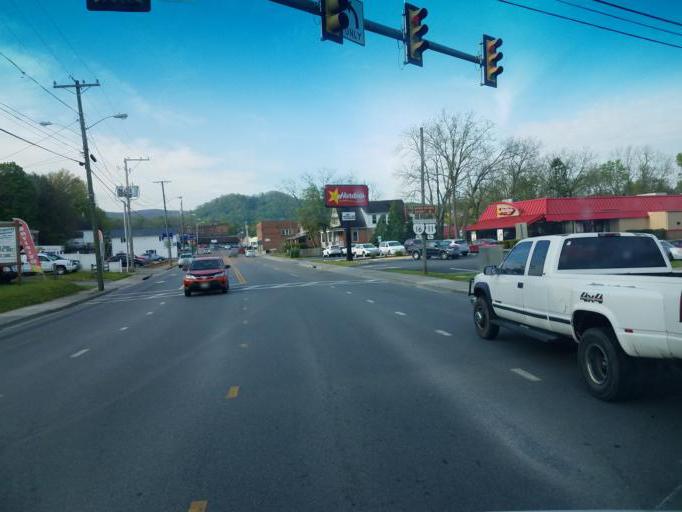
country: US
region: Virginia
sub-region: Smyth County
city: Marion
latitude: 36.8367
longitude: -81.5158
